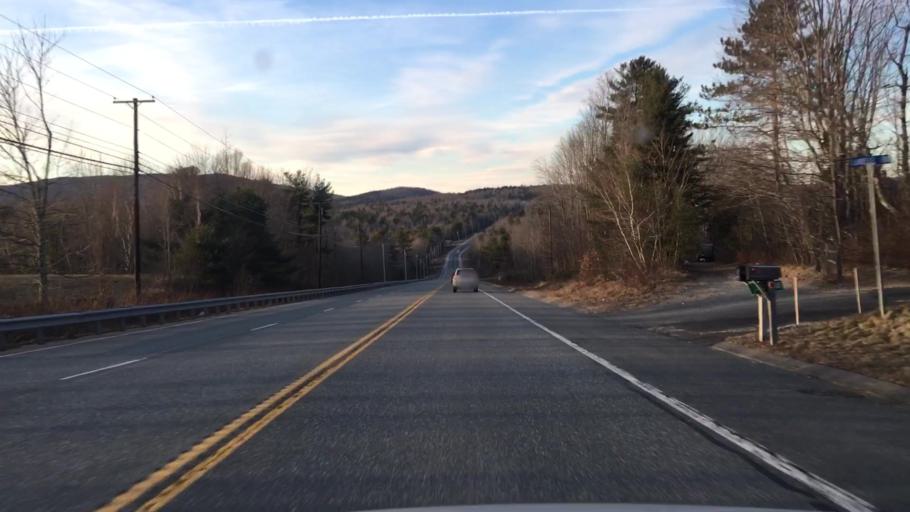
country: US
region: Maine
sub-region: Hancock County
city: Surry
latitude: 44.6283
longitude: -68.5379
